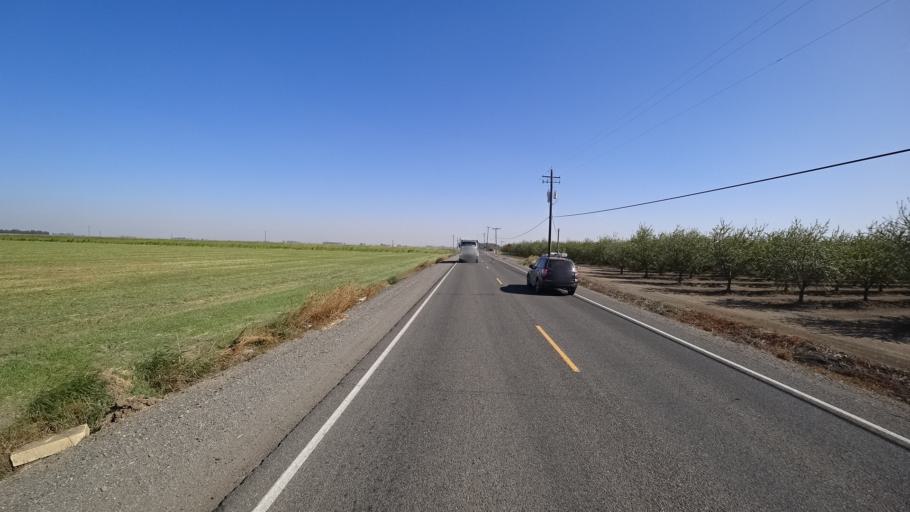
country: US
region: California
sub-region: Yolo County
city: Davis
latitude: 38.5905
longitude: -121.7556
